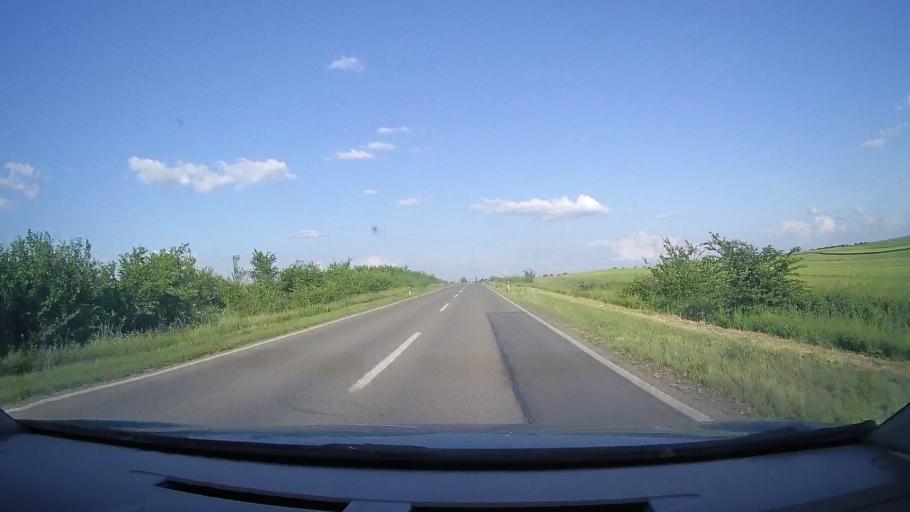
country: RS
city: Uljma
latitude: 45.0468
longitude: 21.1292
